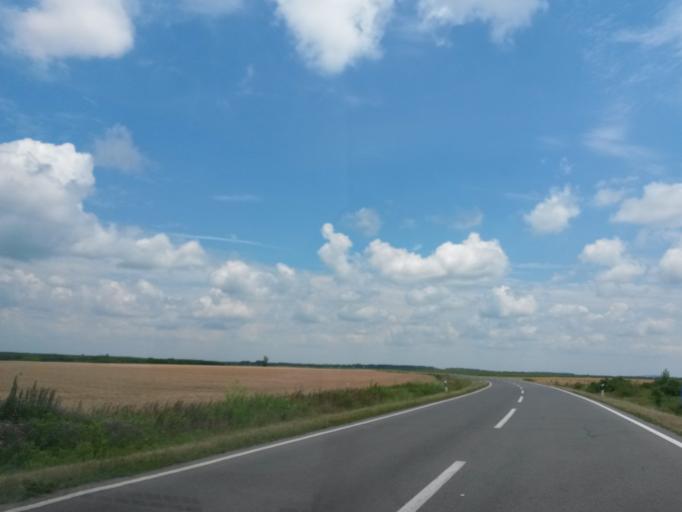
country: HR
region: Osjecko-Baranjska
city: Sarvas
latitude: 45.5242
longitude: 18.7923
